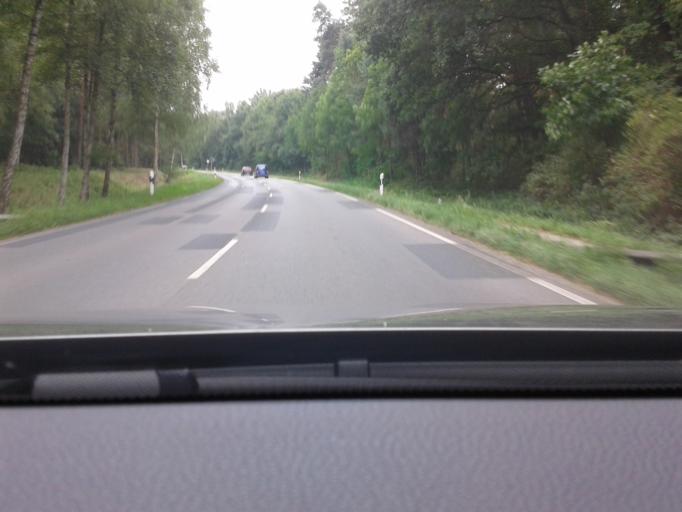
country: DE
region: Lower Saxony
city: Gifhorn
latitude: 52.4915
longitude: 10.5689
